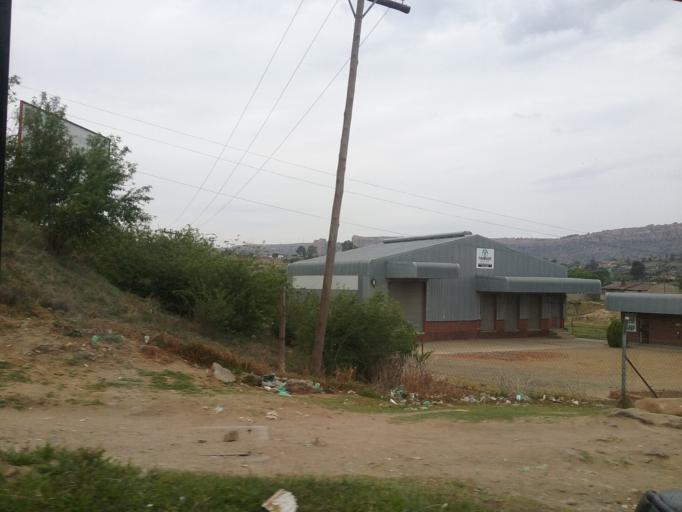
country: LS
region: Maseru
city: Maseru
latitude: -29.3167
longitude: 27.5095
